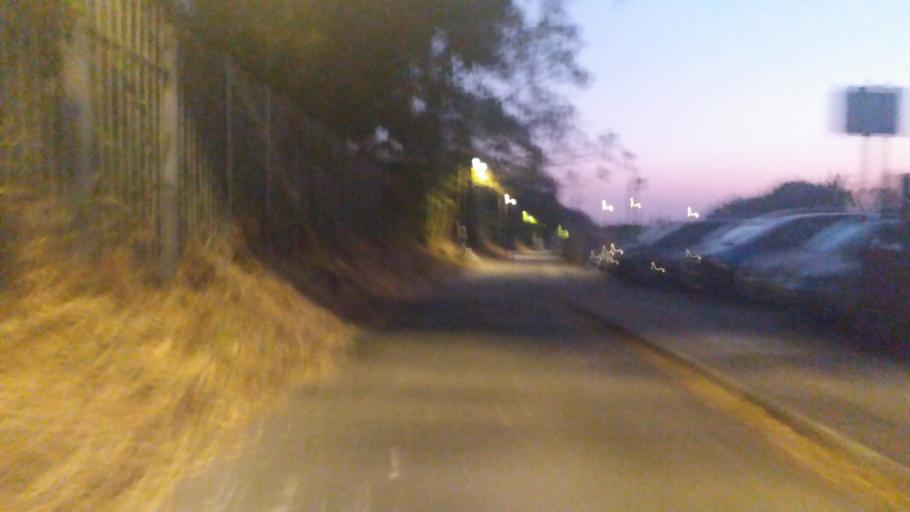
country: HK
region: Yuen Long
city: Yuen Long Kau Hui
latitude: 22.4488
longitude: 113.9986
